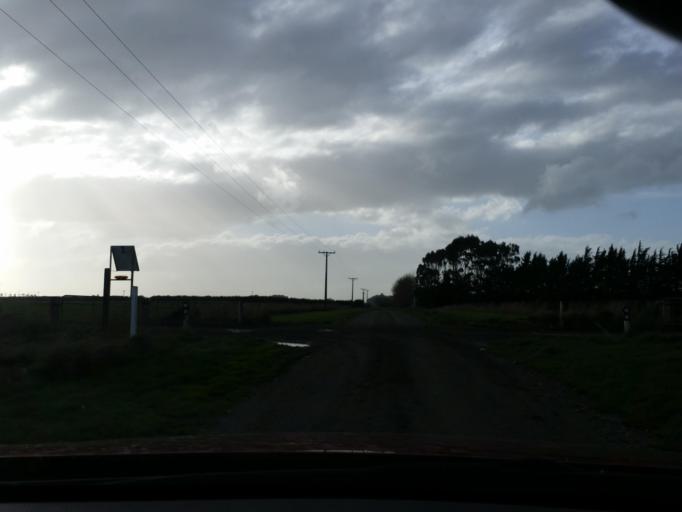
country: NZ
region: Southland
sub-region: Southland District
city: Winton
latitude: -46.2427
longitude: 168.3222
